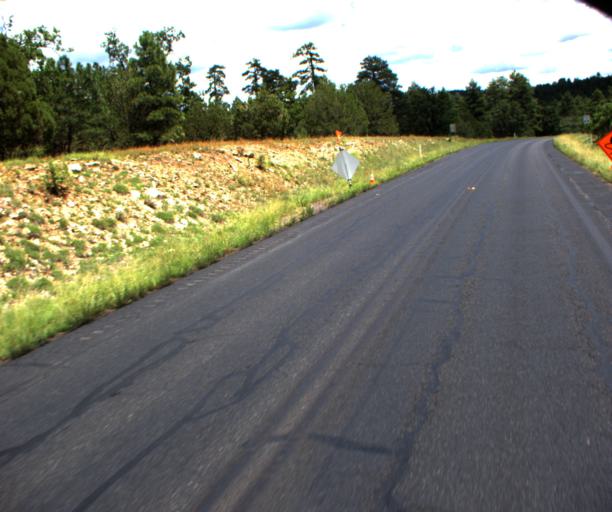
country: US
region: Arizona
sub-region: Gila County
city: Pine
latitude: 34.5213
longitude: -111.5127
